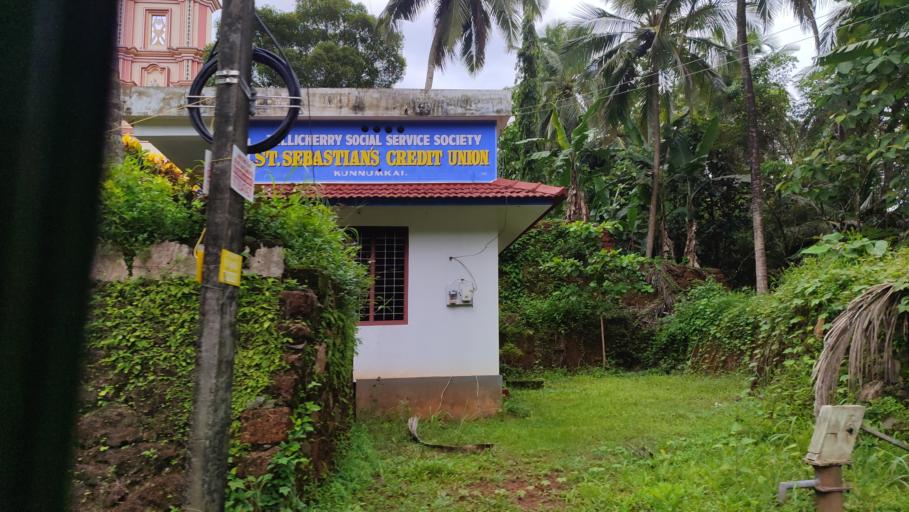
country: IN
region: Kerala
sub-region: Kasaragod District
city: Nileshwar
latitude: 12.2971
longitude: 75.2921
